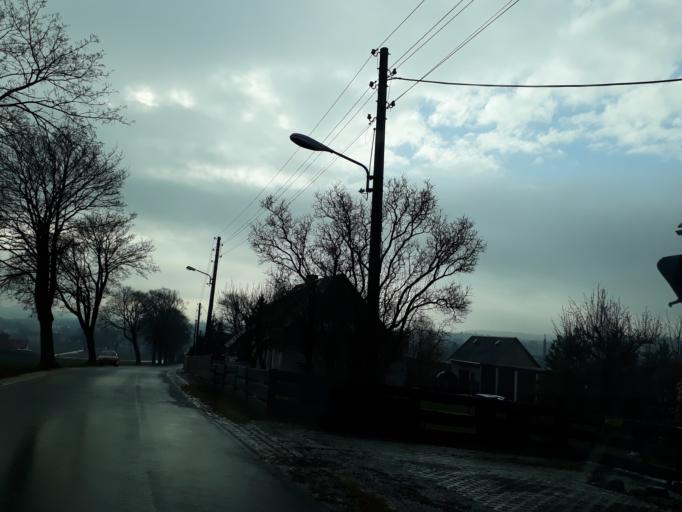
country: DE
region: Saxony
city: Eibau
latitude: 50.9927
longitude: 14.6646
